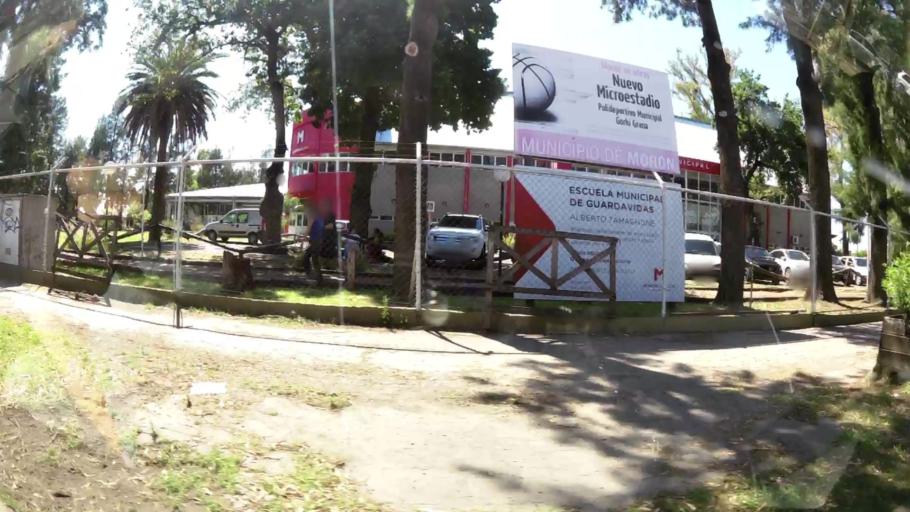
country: AR
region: Buenos Aires
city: Ituzaingo
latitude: -34.6593
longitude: -58.6607
